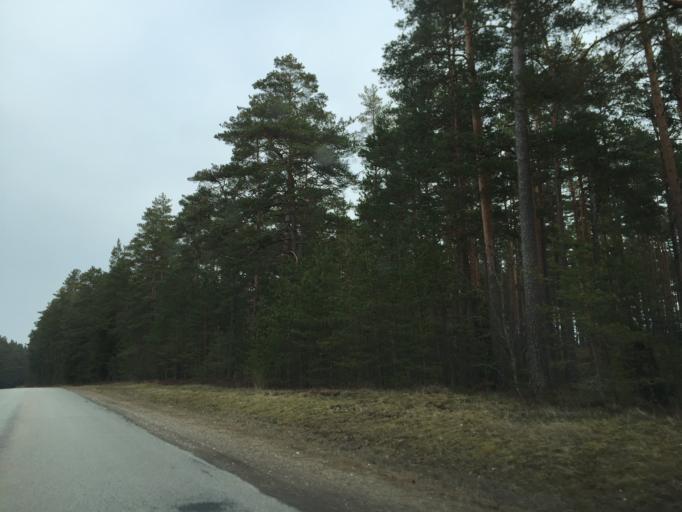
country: LV
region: Salacgrivas
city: Ainazi
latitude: 57.9797
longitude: 24.4158
